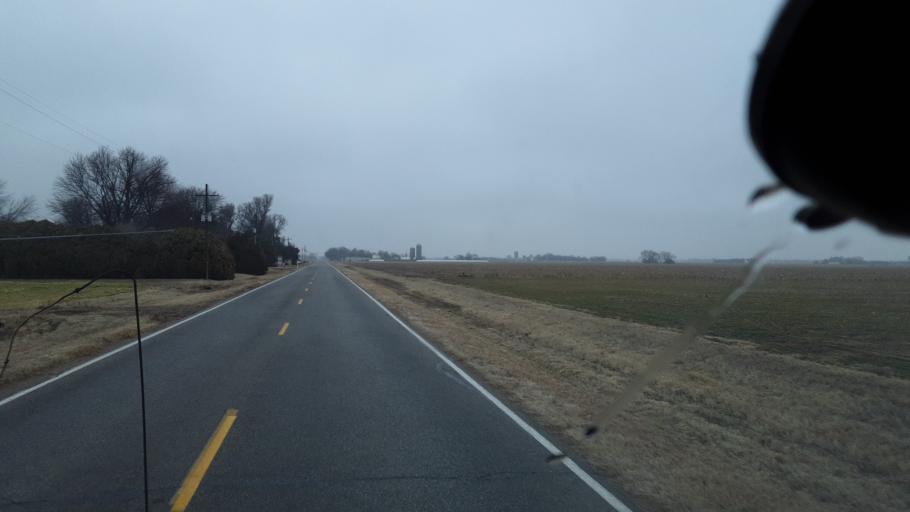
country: US
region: Kansas
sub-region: Reno County
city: South Hutchinson
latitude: 37.9728
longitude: -98.0138
